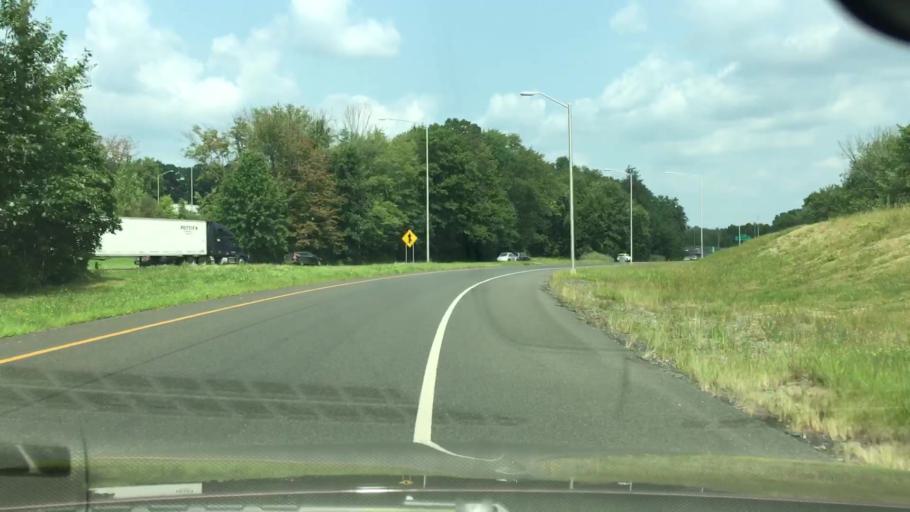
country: US
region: Connecticut
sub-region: New Haven County
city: Cheshire Village
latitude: 41.5784
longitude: -72.9008
